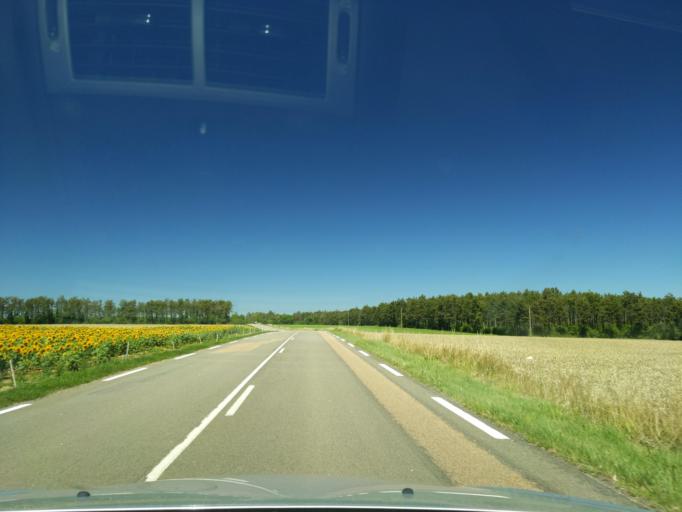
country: FR
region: Bourgogne
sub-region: Departement de la Cote-d'Or
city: Is-sur-Tille
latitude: 47.5007
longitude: 5.0841
